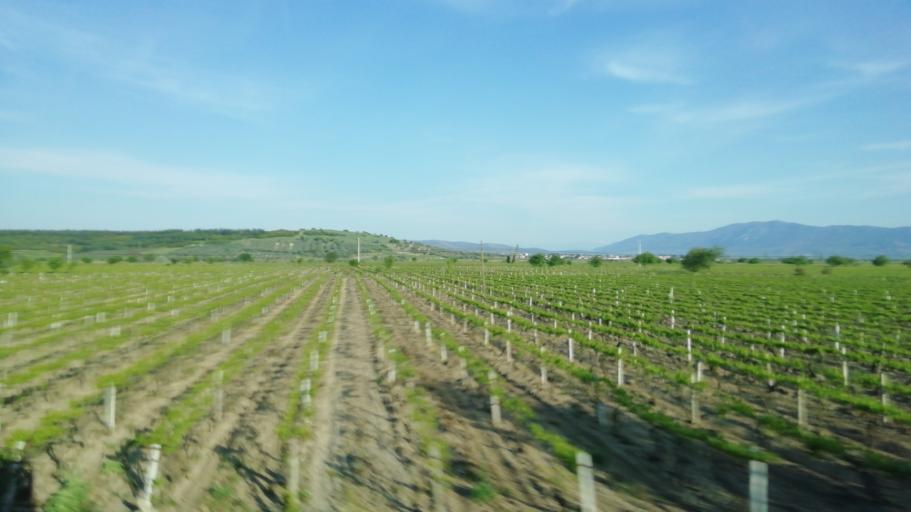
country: TR
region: Manisa
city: Halitpasa
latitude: 38.7783
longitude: 27.6650
